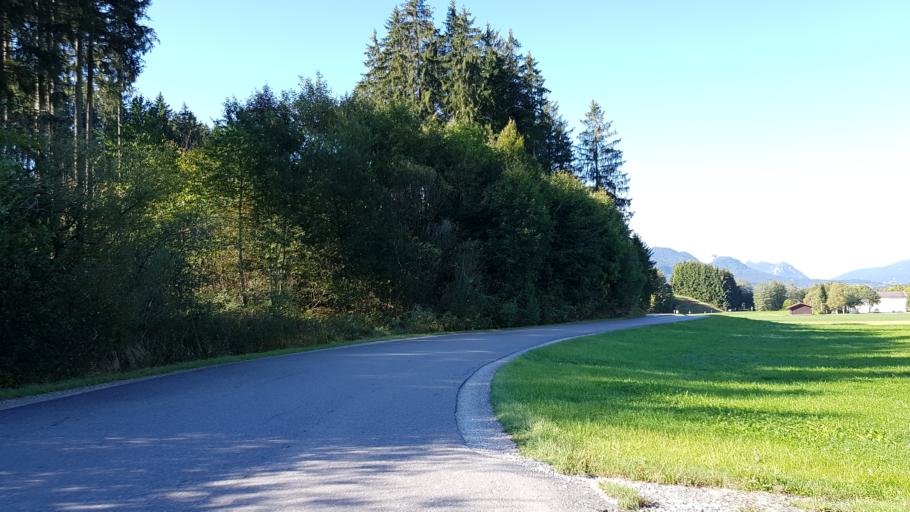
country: DE
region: Bavaria
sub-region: Swabia
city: Fuessen
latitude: 47.5793
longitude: 10.6847
